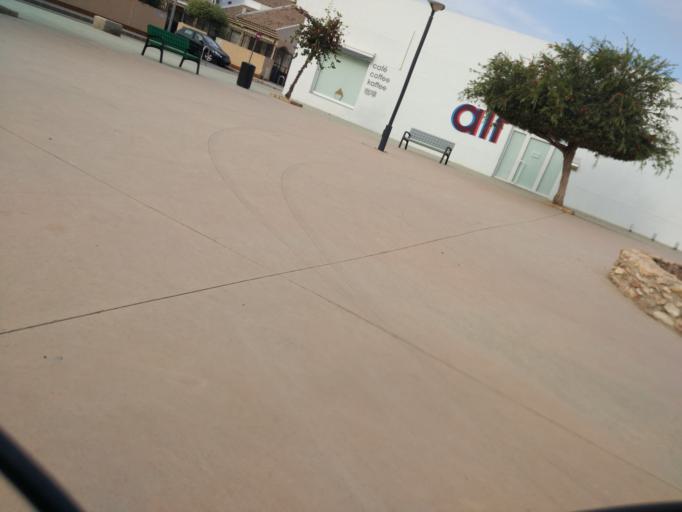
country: ES
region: Murcia
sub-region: Murcia
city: Los Alcazares
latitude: 37.7474
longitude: -0.8542
